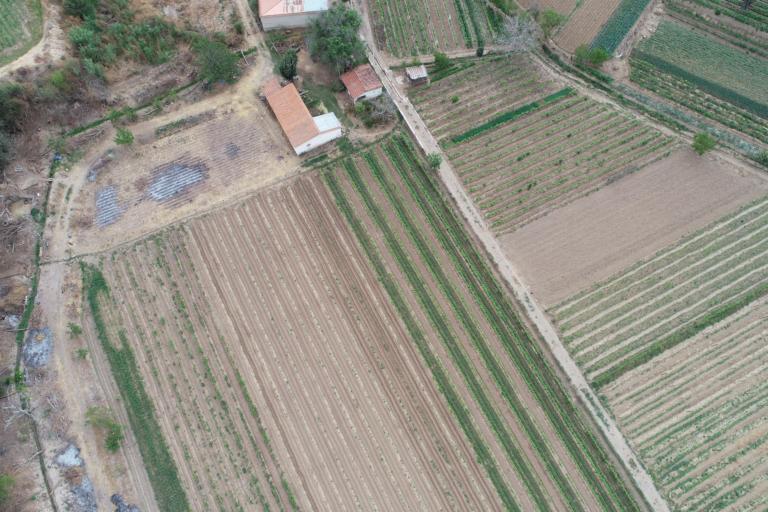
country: BO
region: Tarija
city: Tarija
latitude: -21.6002
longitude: -64.6178
